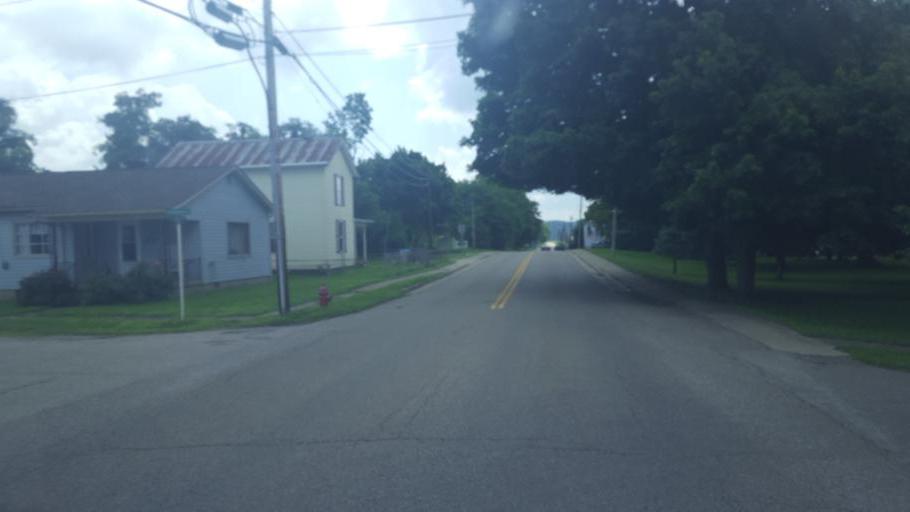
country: US
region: Ohio
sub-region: Ross County
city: Kingston
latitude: 39.4696
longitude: -82.7364
